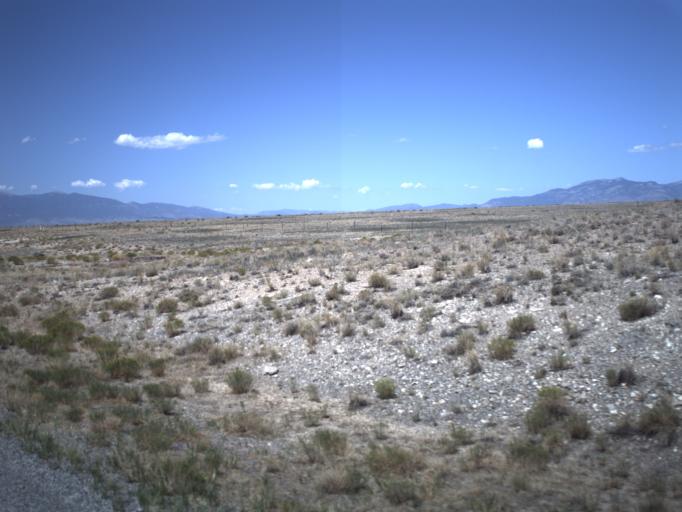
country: US
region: Utah
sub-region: Beaver County
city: Milford
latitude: 39.0408
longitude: -113.8117
